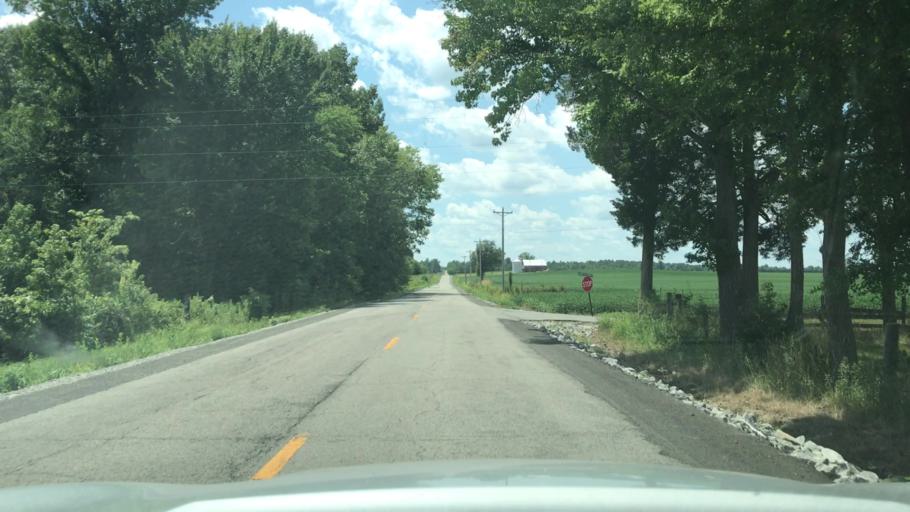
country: US
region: Kentucky
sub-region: Muhlenberg County
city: Greenville
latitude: 37.1324
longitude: -87.2817
